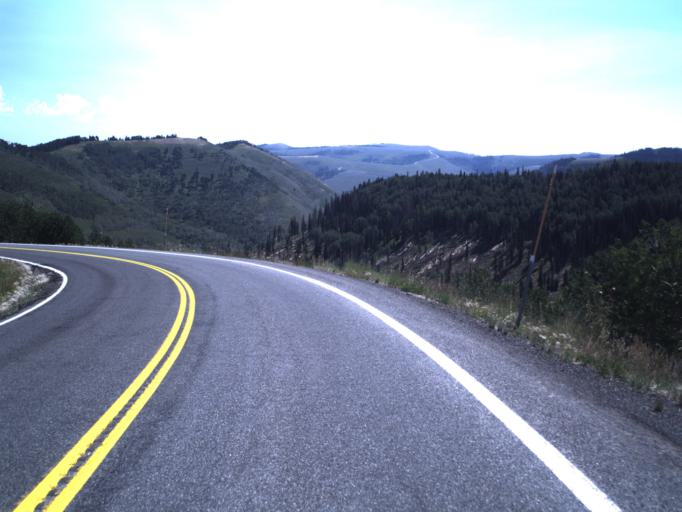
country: US
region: Utah
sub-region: Sanpete County
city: Fairview
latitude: 39.6799
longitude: -111.2166
